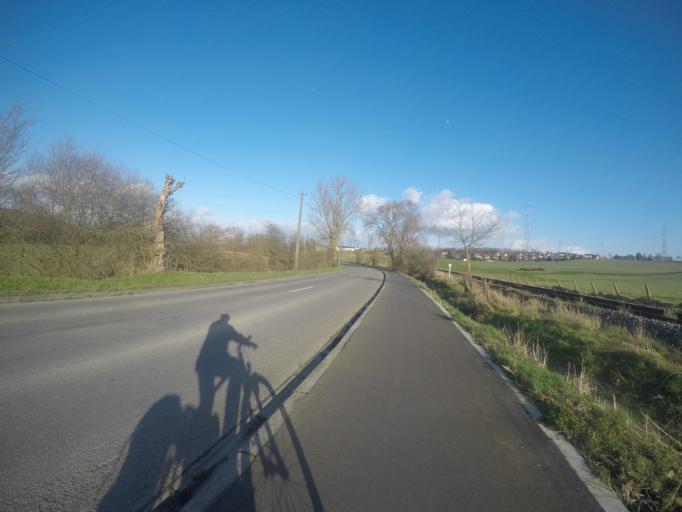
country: BE
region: Wallonia
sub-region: Province du Brabant Wallon
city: Tubize
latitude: 50.6762
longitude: 4.1777
